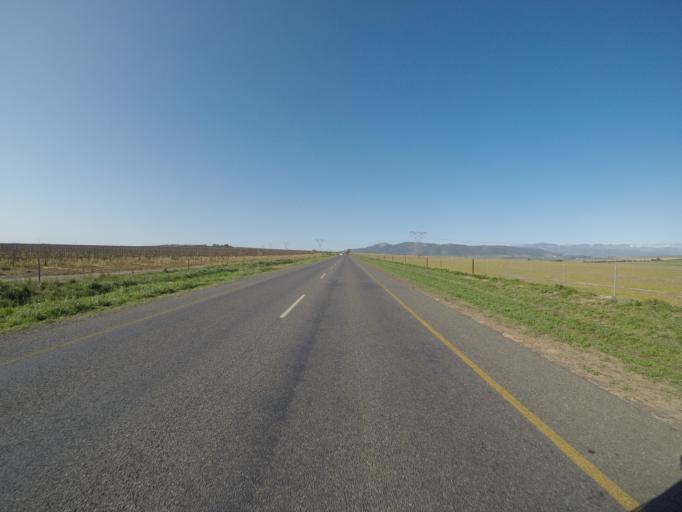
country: ZA
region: Western Cape
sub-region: City of Cape Town
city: Kraaifontein
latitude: -33.7557
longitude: 18.8164
